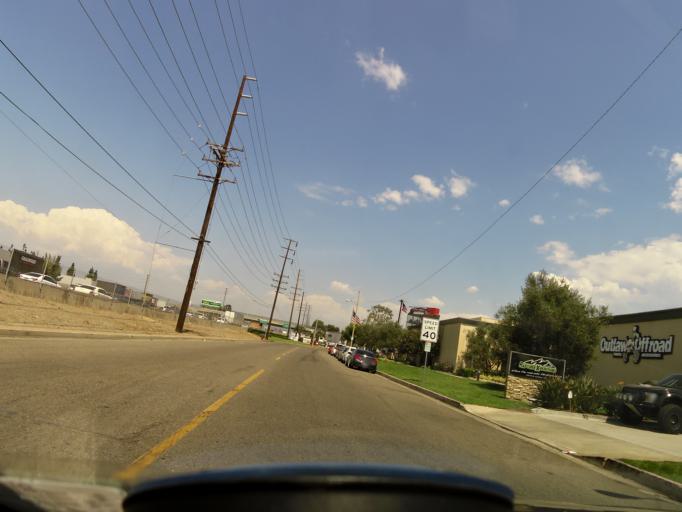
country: US
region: California
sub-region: Orange County
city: Santa Ana
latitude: 33.7128
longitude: -117.8471
